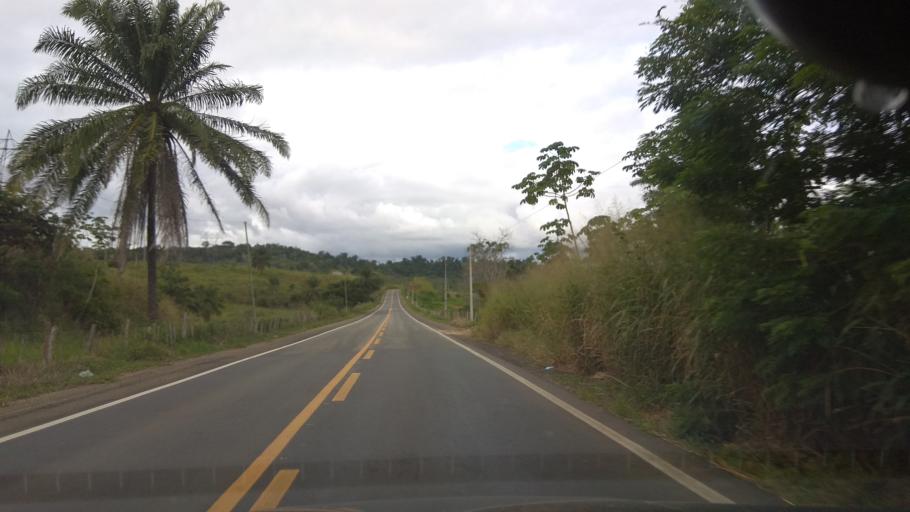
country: BR
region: Bahia
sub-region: Ipiau
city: Ipiau
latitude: -14.1771
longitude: -39.6724
